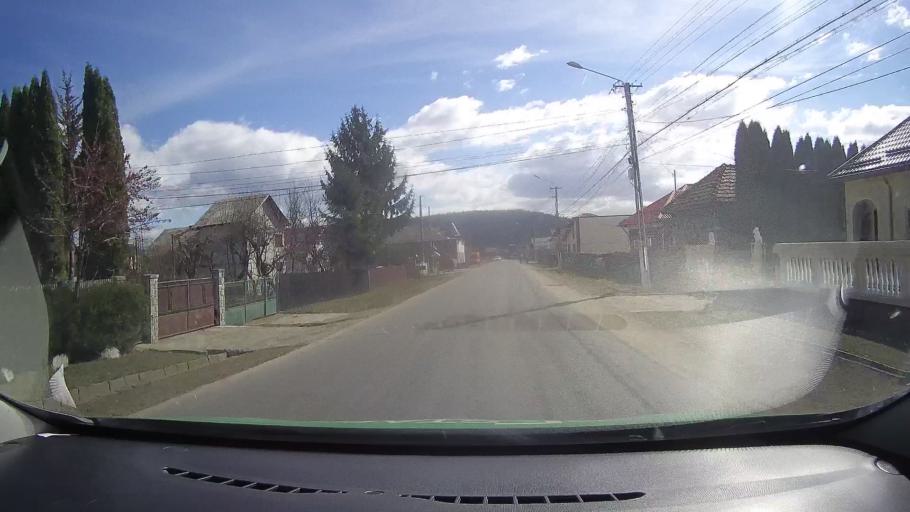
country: RO
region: Dambovita
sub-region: Comuna Vulcana-Pandele
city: Gura Vulcanei
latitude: 45.0228
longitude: 25.3964
